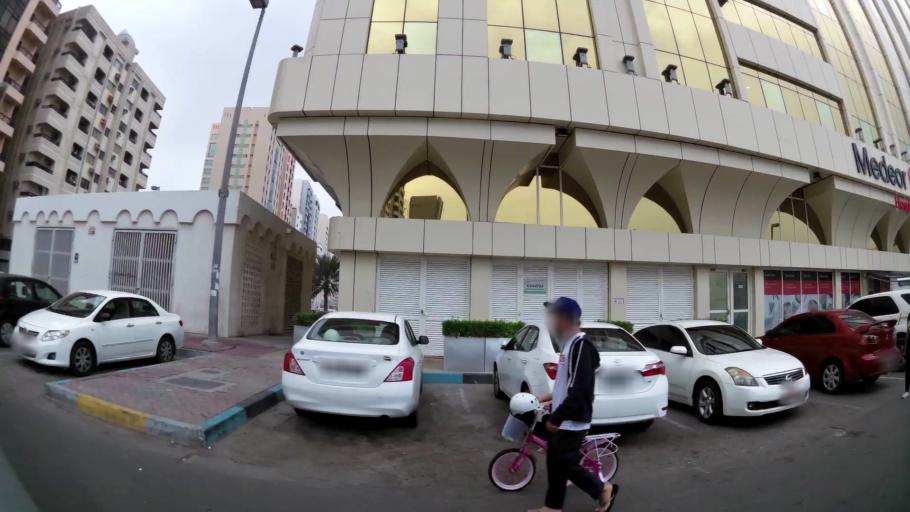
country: AE
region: Abu Dhabi
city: Abu Dhabi
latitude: 24.4804
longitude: 54.3699
